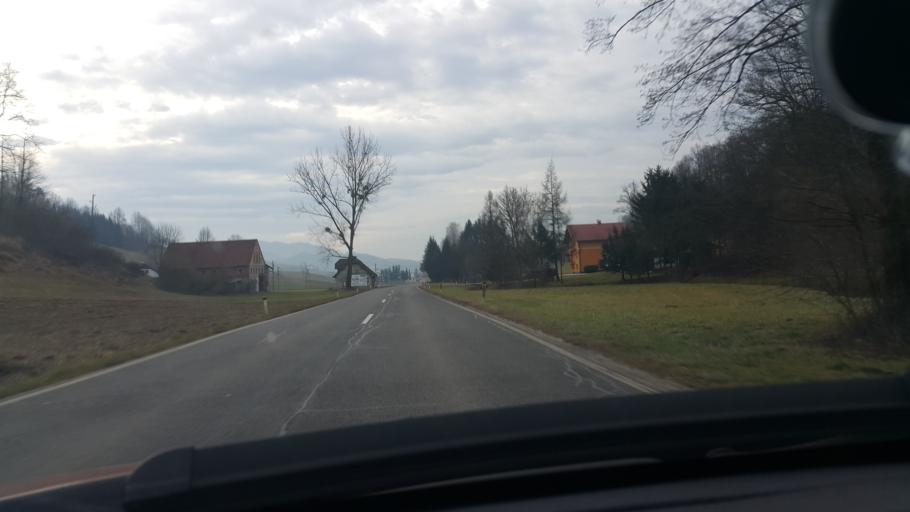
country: SI
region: Podcetrtek
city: Podcetrtek
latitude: 46.2069
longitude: 15.5900
